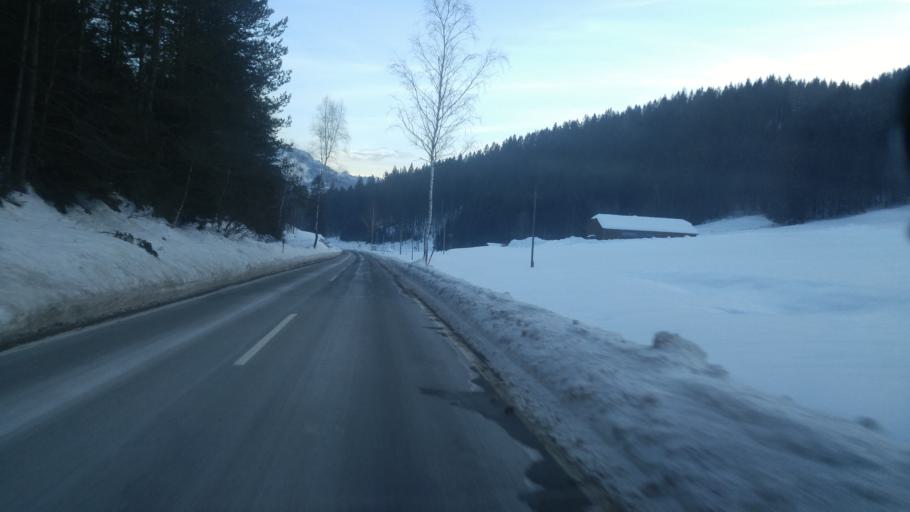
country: AT
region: Lower Austria
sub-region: Politischer Bezirk Wiener Neustadt
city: Rohr im Gebirge
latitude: 47.8742
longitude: 15.6968
